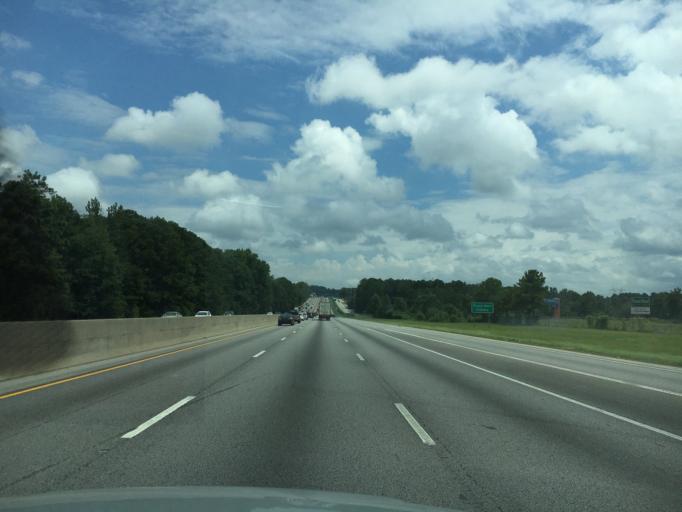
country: US
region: Georgia
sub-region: DeKalb County
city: Lithonia
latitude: 33.6981
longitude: -84.0844
